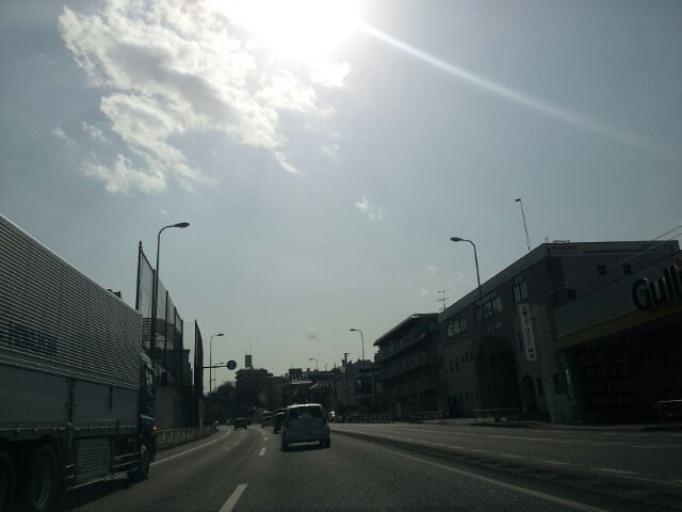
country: JP
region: Kanagawa
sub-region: Kawasaki-shi
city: Kawasaki
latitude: 35.5146
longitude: 139.6648
